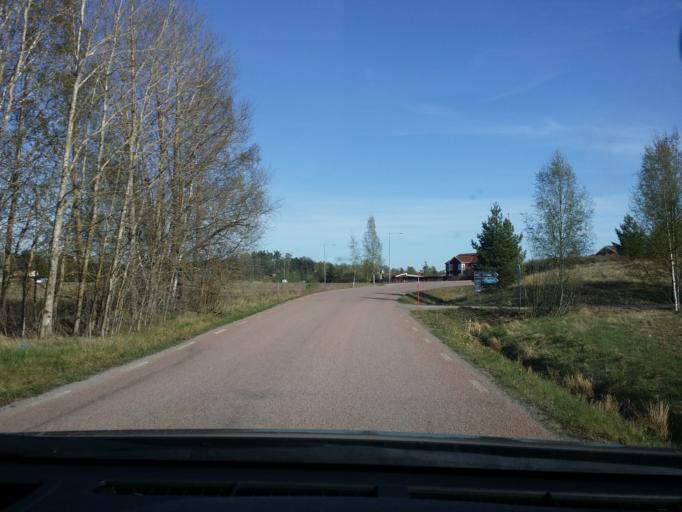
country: SE
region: Vaestmanland
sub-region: Vasteras
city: Vasteras
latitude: 59.6347
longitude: 16.4881
